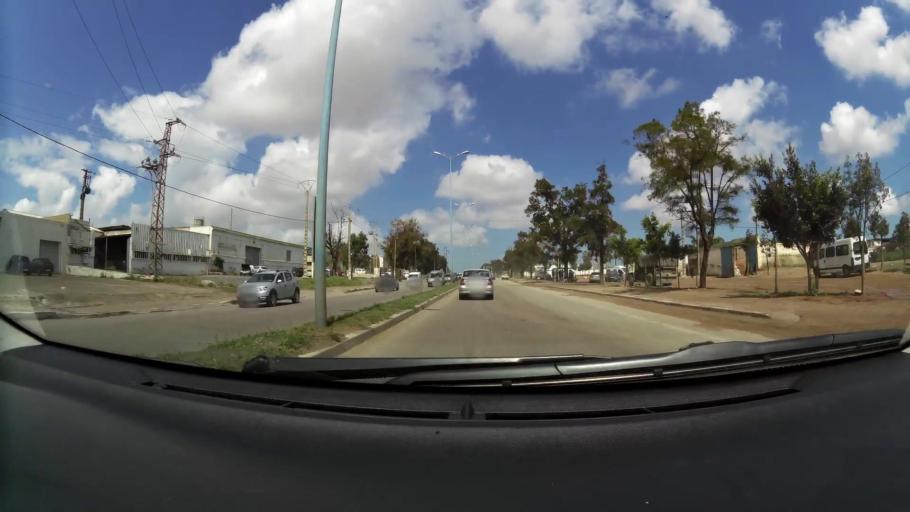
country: MA
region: Grand Casablanca
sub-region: Casablanca
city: Casablanca
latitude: 33.5309
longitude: -7.5689
